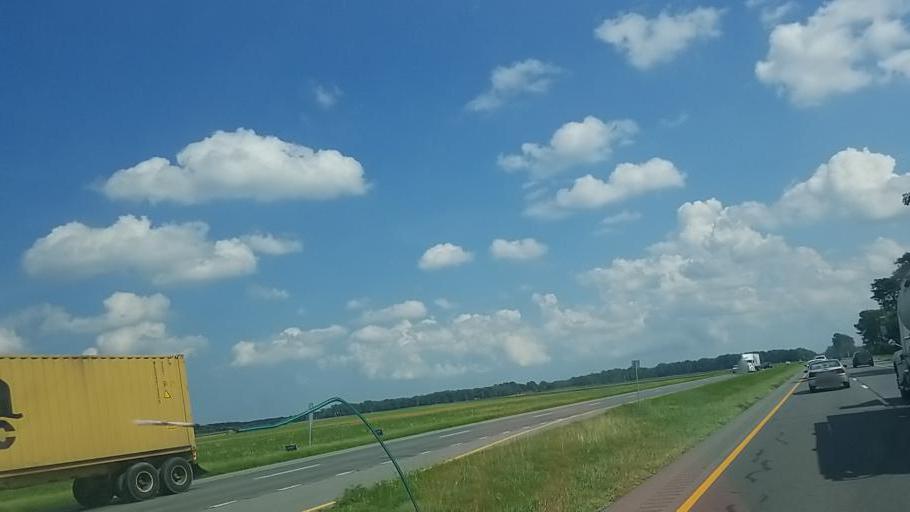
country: US
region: Delaware
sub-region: Sussex County
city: Millsboro
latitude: 38.6252
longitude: -75.3420
